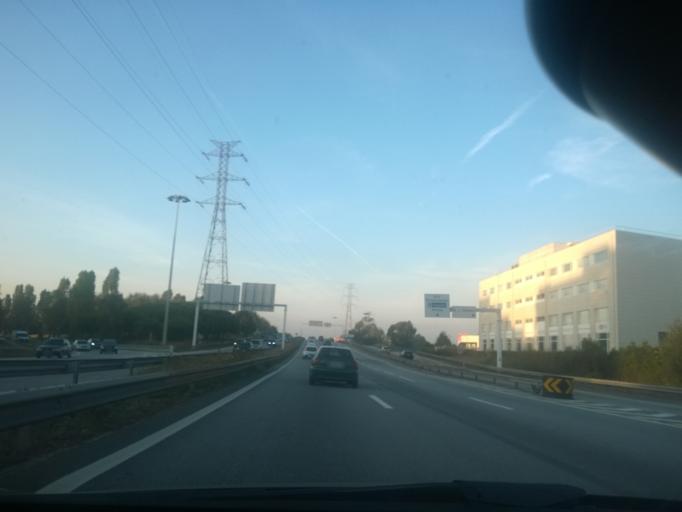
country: PT
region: Porto
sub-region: Matosinhos
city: Sao Mamede de Infesta
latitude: 41.1787
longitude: -8.6223
